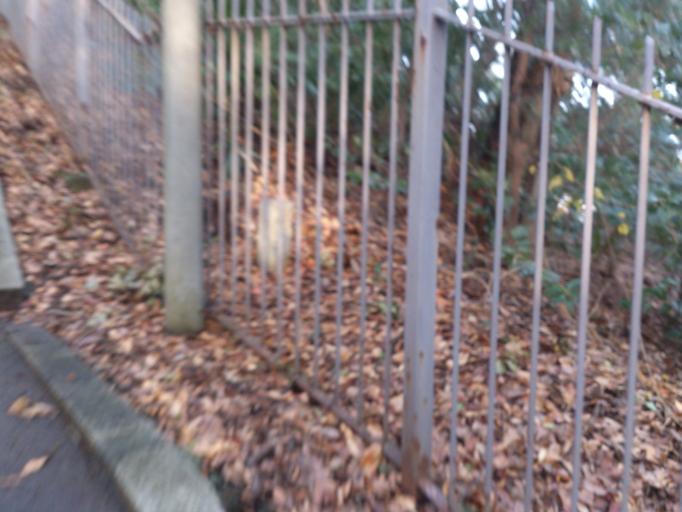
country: JP
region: Chiba
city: Matsudo
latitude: 35.7734
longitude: 139.8975
